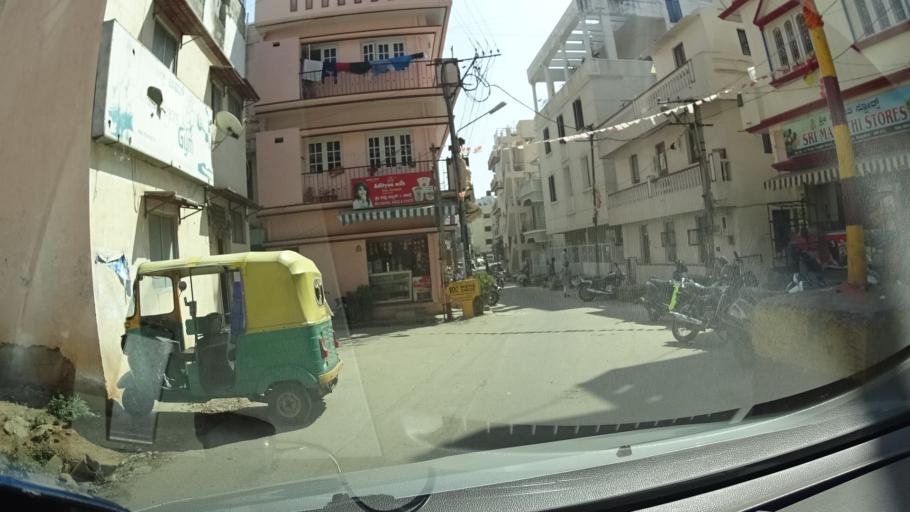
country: IN
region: Karnataka
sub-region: Bangalore Urban
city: Bangalore
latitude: 12.9624
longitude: 77.6353
